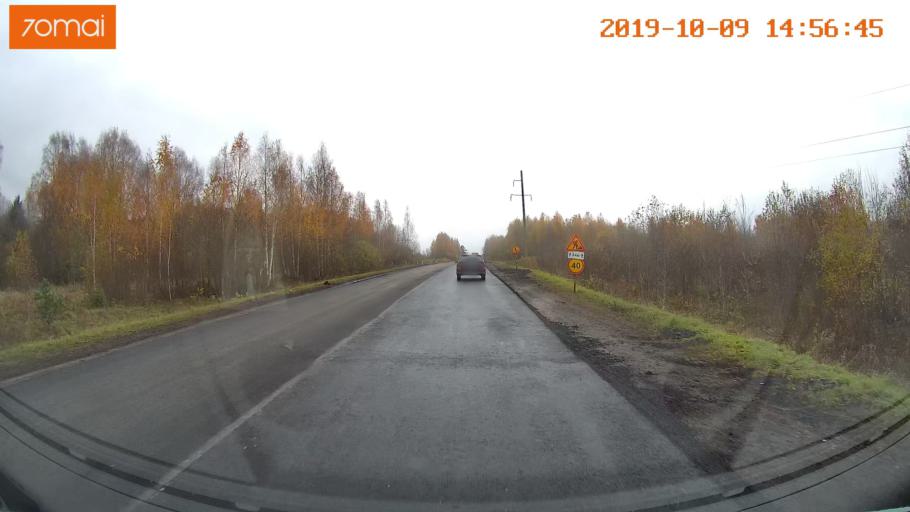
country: RU
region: Kostroma
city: Chistyye Bory
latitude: 58.3434
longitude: 41.6484
